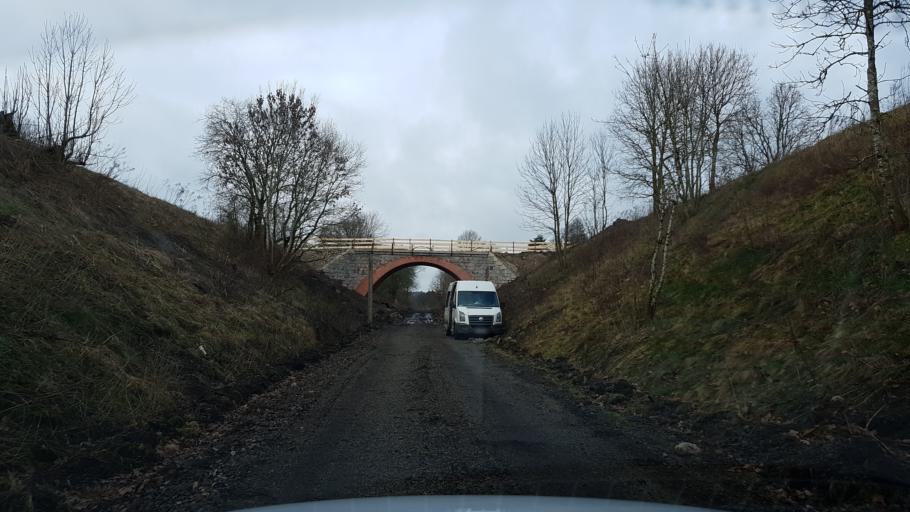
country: PL
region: West Pomeranian Voivodeship
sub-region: Powiat swidwinski
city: Polczyn-Zdroj
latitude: 53.7861
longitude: 16.0531
